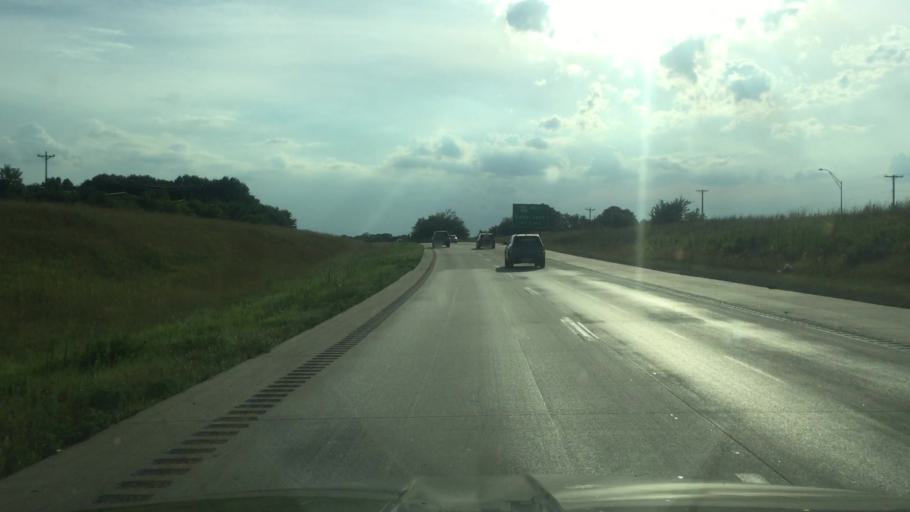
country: US
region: Missouri
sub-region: Jackson County
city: Lone Jack
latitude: 38.8711
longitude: -94.1510
